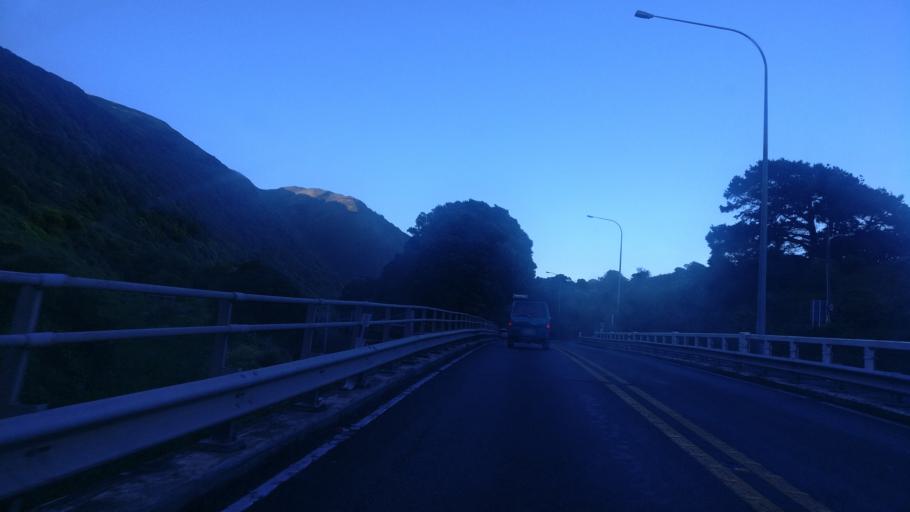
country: NZ
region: Wellington
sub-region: Kapiti Coast District
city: Paraparaumu
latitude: -40.9936
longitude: 174.9470
